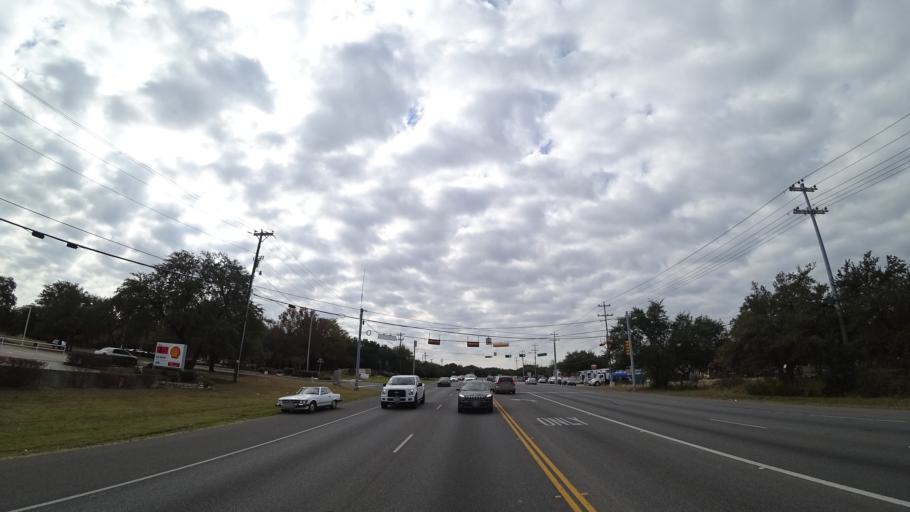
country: US
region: Texas
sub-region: Williamson County
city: Anderson Mill
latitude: 30.4439
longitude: -97.8329
